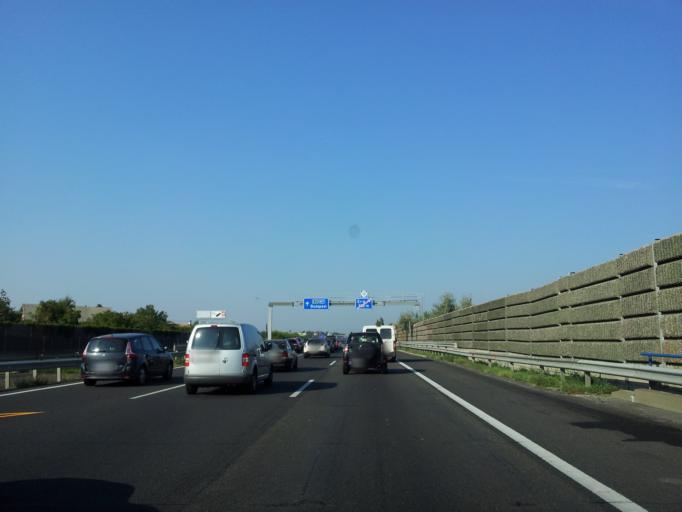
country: HU
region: Pest
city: Erd
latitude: 47.4071
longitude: 18.8758
